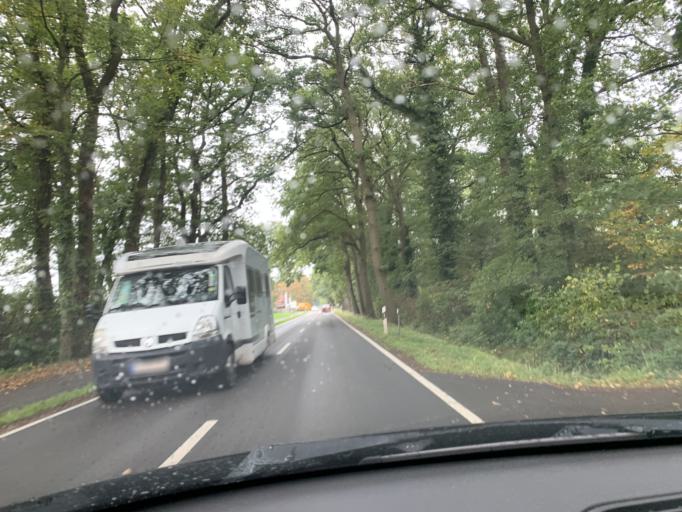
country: DE
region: Lower Saxony
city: Bad Zwischenahn
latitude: 53.1612
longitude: 8.0790
